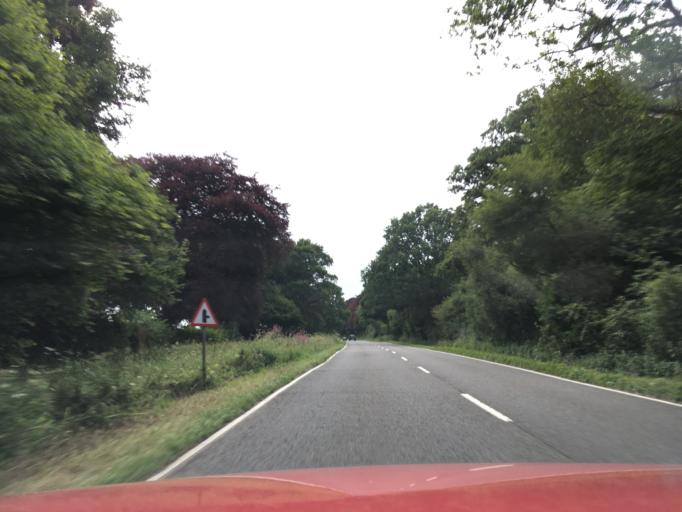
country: GB
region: England
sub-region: Hampshire
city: Four Marks
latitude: 51.0423
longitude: -1.1068
